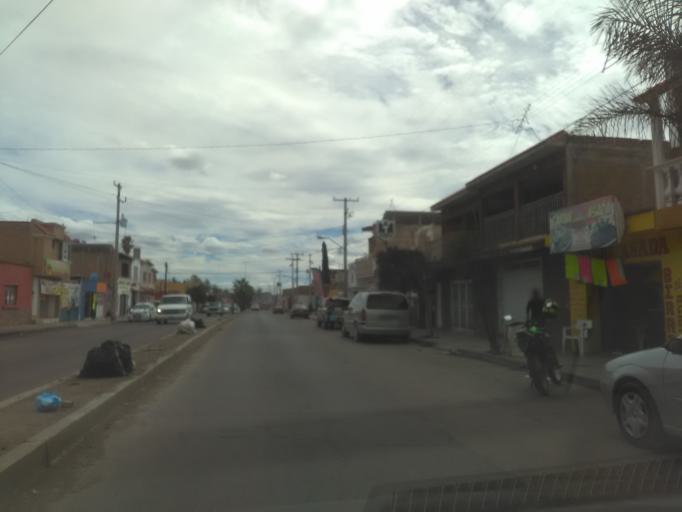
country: MX
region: Durango
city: Victoria de Durango
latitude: 24.0476
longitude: -104.6848
